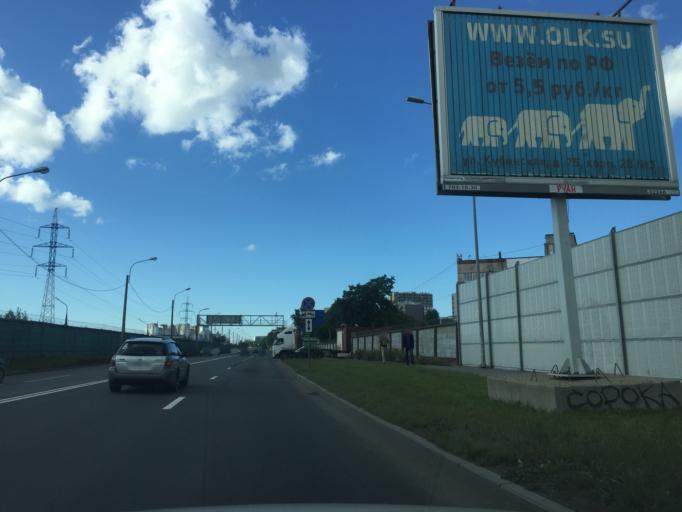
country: RU
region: St.-Petersburg
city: Dachnoye
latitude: 59.8358
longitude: 30.3055
